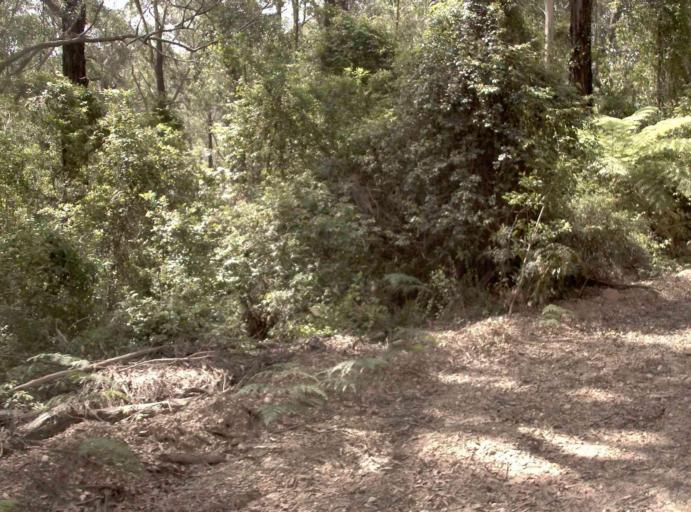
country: AU
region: Victoria
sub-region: East Gippsland
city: Lakes Entrance
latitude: -37.5868
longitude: 148.7258
